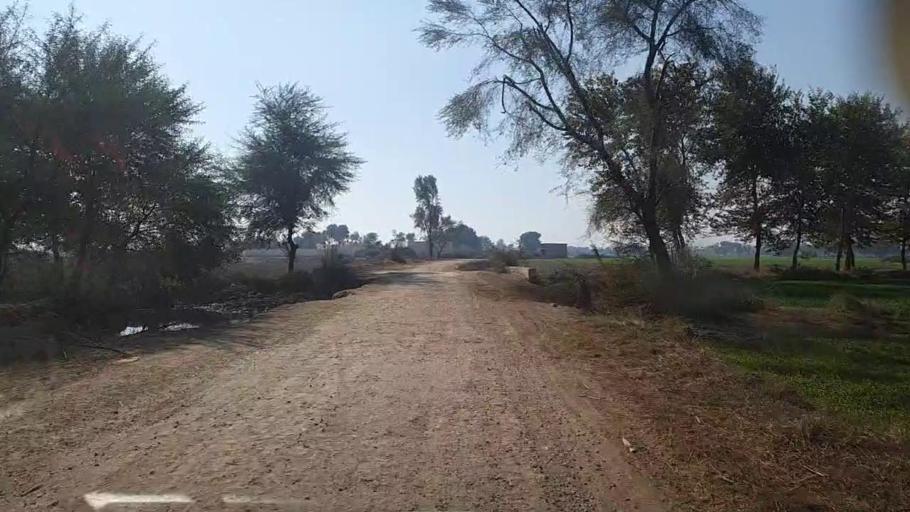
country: PK
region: Sindh
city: Khairpur
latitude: 28.0498
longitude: 69.7791
